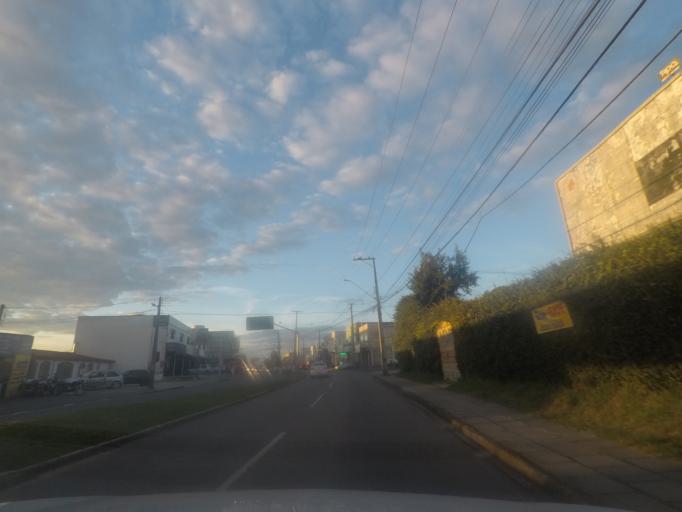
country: BR
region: Parana
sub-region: Pinhais
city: Pinhais
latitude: -25.4318
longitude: -49.1839
